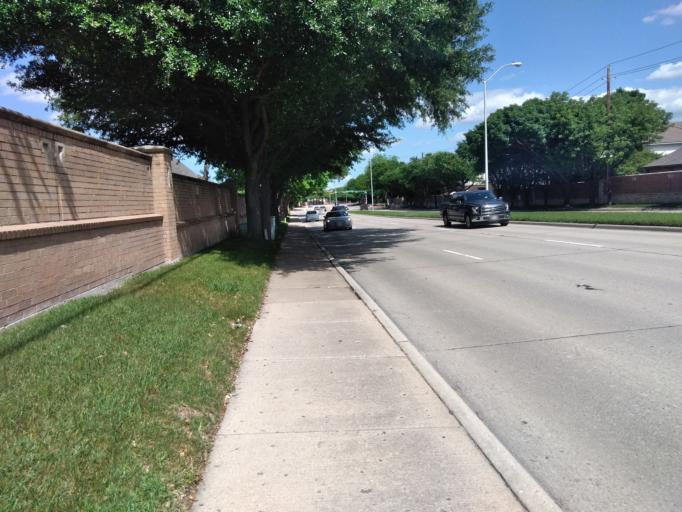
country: US
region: Texas
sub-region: Dallas County
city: Addison
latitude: 32.9993
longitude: -96.8199
